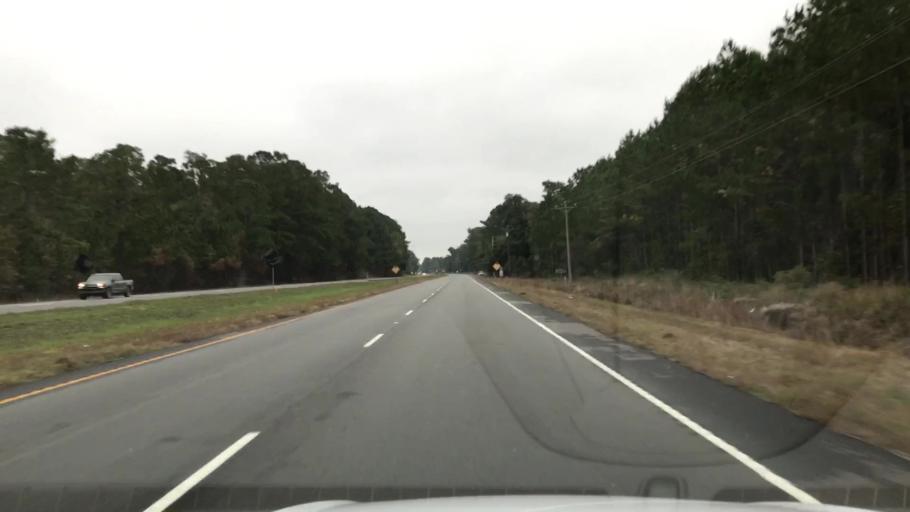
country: US
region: South Carolina
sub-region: Charleston County
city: Awendaw
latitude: 33.0868
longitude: -79.4899
